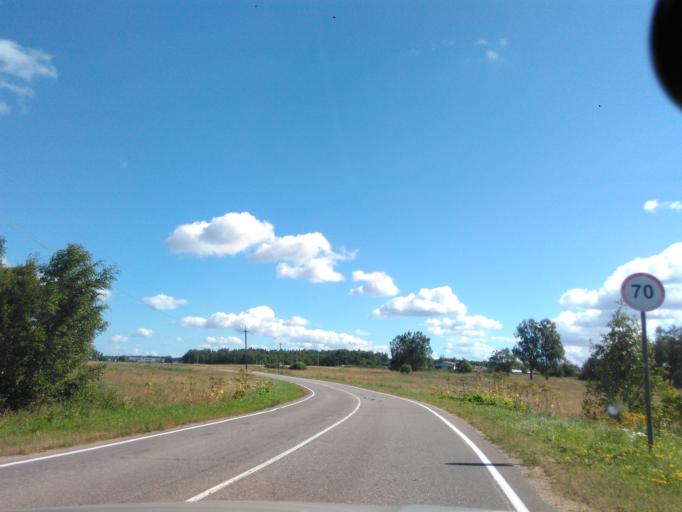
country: RU
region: Moskovskaya
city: Klin
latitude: 56.1829
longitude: 36.8064
